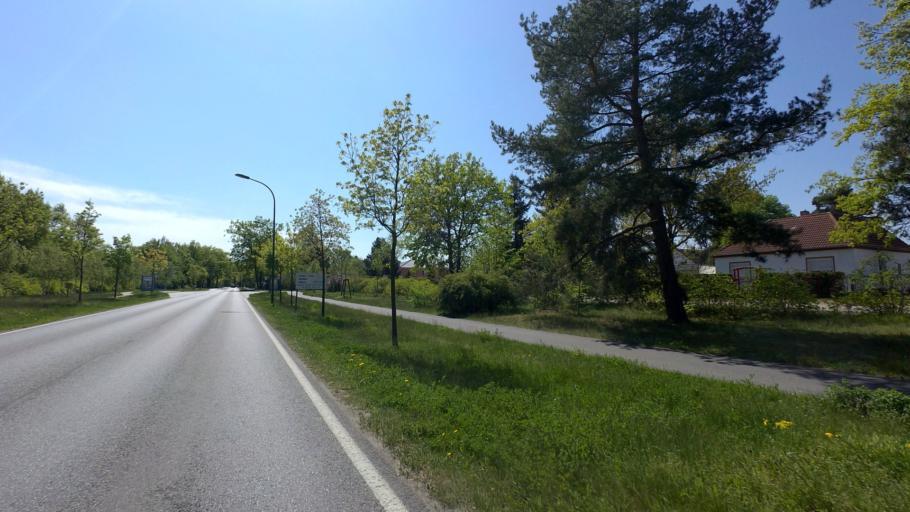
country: DE
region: Brandenburg
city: Bestensee
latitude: 52.2701
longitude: 13.6332
